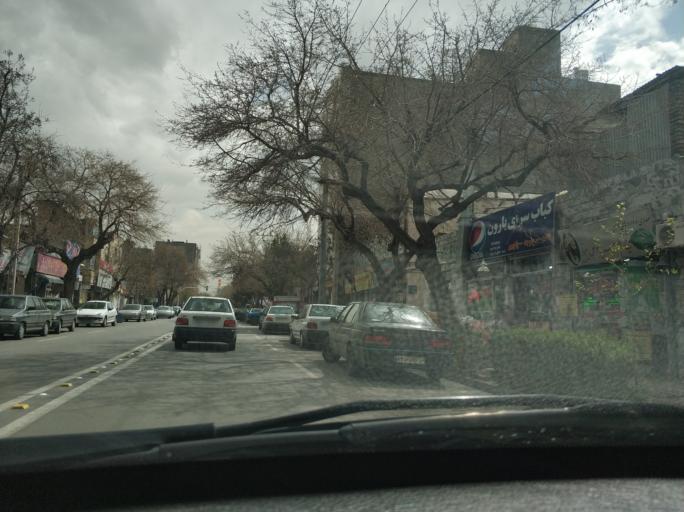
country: IR
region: Razavi Khorasan
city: Mashhad
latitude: 36.2813
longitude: 59.5731
